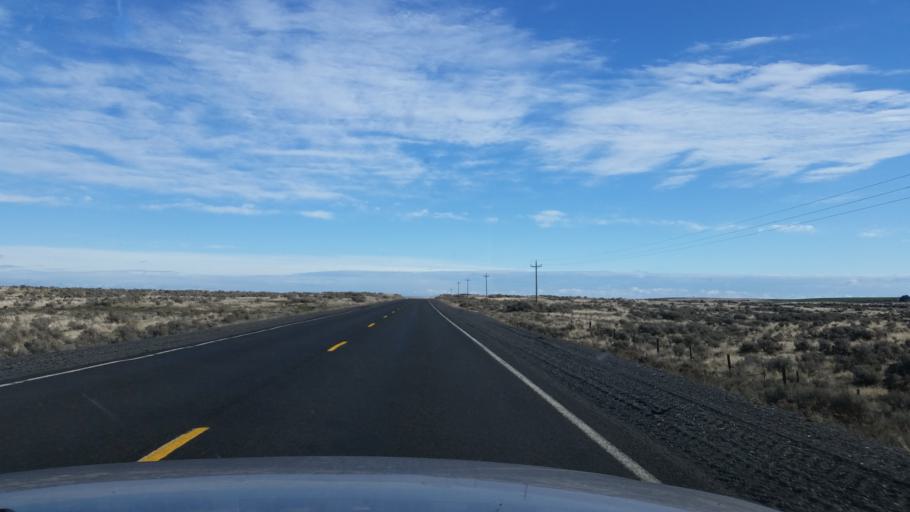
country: US
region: Washington
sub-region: Grant County
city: Warden
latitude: 47.3147
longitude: -118.7978
